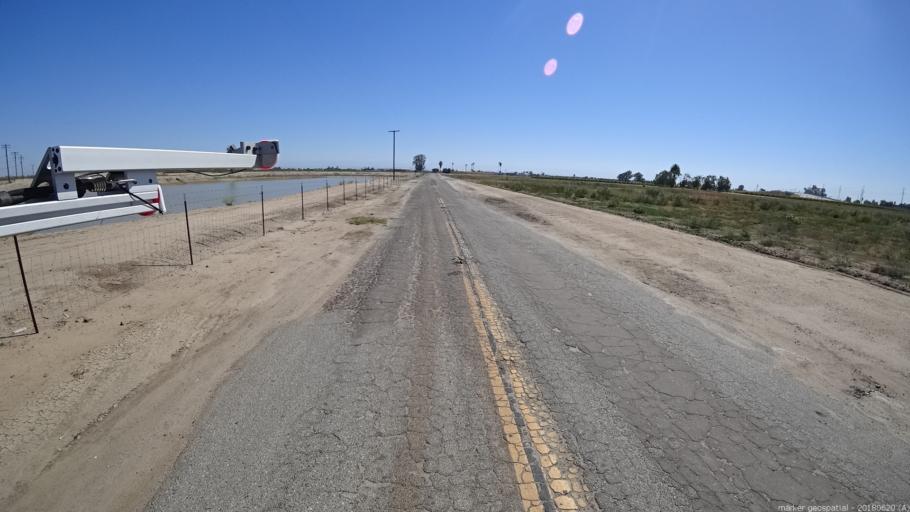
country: US
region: California
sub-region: Madera County
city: Parkwood
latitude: 36.9258
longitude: -120.0331
